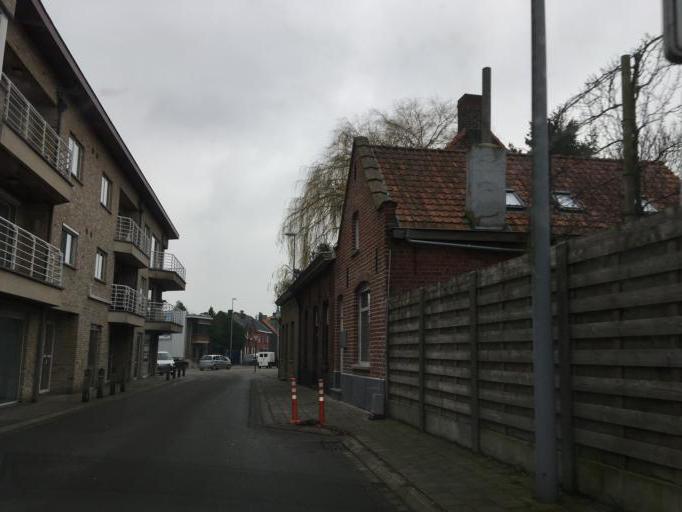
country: BE
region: Flanders
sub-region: Provincie West-Vlaanderen
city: Roeselare
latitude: 50.9713
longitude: 3.1417
